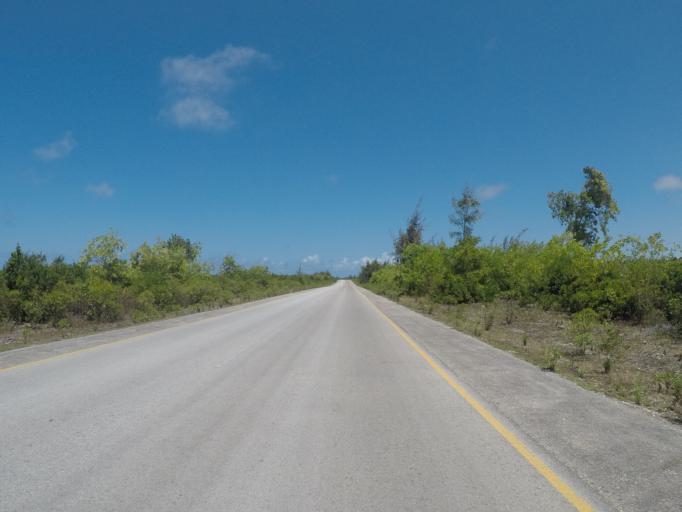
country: TZ
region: Zanzibar Central/South
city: Nganane
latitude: -6.4007
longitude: 39.5614
